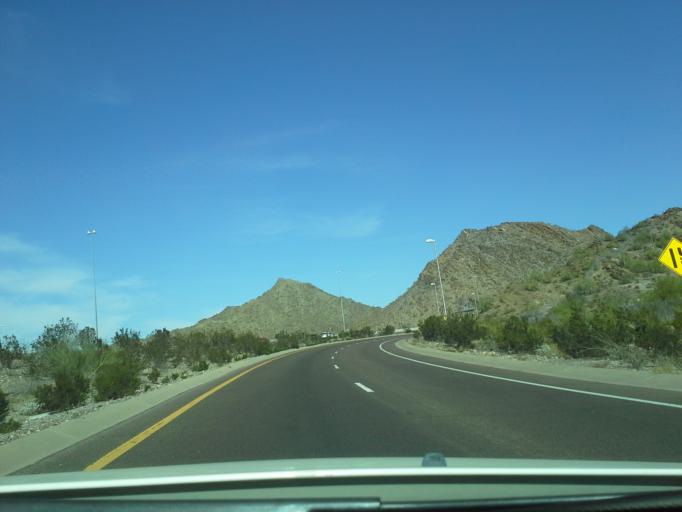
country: US
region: Arizona
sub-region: Maricopa County
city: Paradise Valley
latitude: 33.5601
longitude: -112.0375
